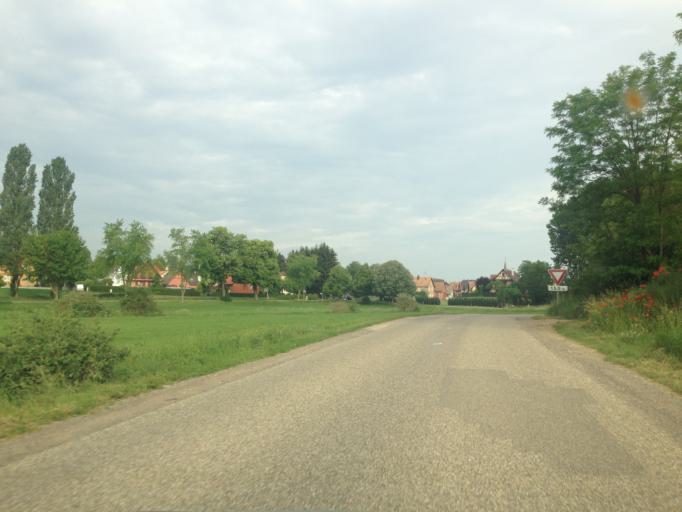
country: FR
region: Alsace
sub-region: Departement du Bas-Rhin
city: Hochfelden
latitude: 48.7792
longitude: 7.5667
